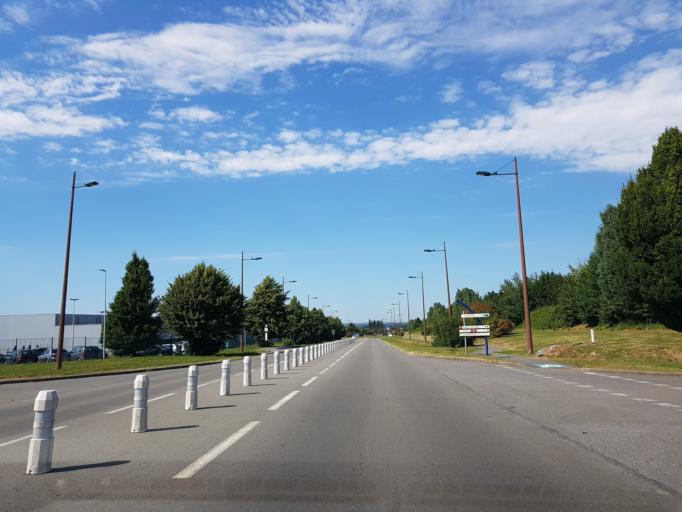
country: FR
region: Nord-Pas-de-Calais
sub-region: Departement du Nord
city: Onnaing
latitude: 50.3658
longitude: 3.6097
